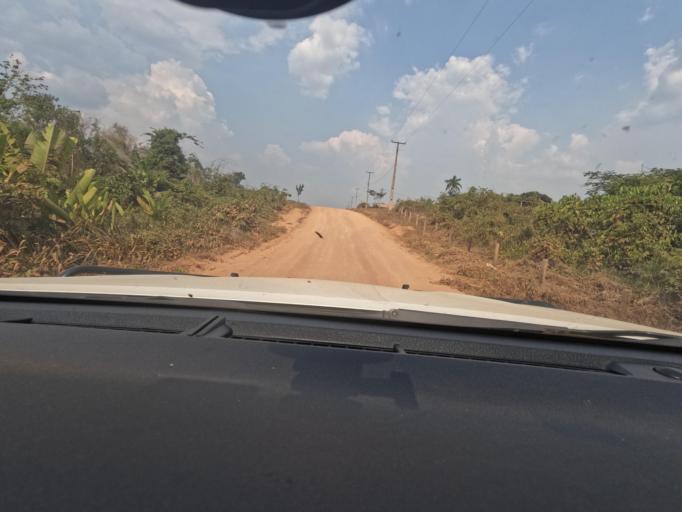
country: BR
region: Rondonia
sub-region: Porto Velho
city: Porto Velho
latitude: -8.6832
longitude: -63.1877
